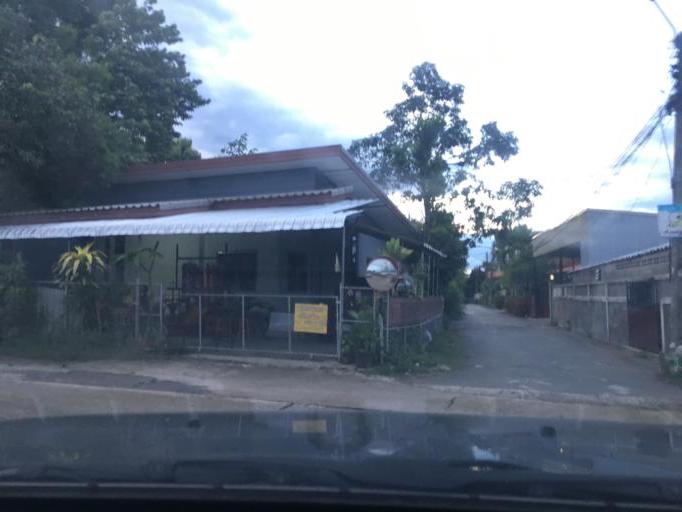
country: TH
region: Chiang Mai
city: San Sai
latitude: 18.8788
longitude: 98.9700
